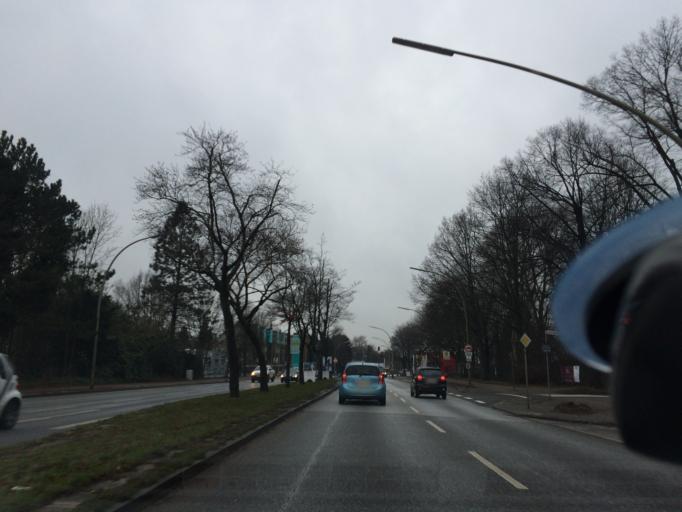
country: DE
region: Hamburg
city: Eidelstedt
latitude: 53.5720
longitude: 9.8574
